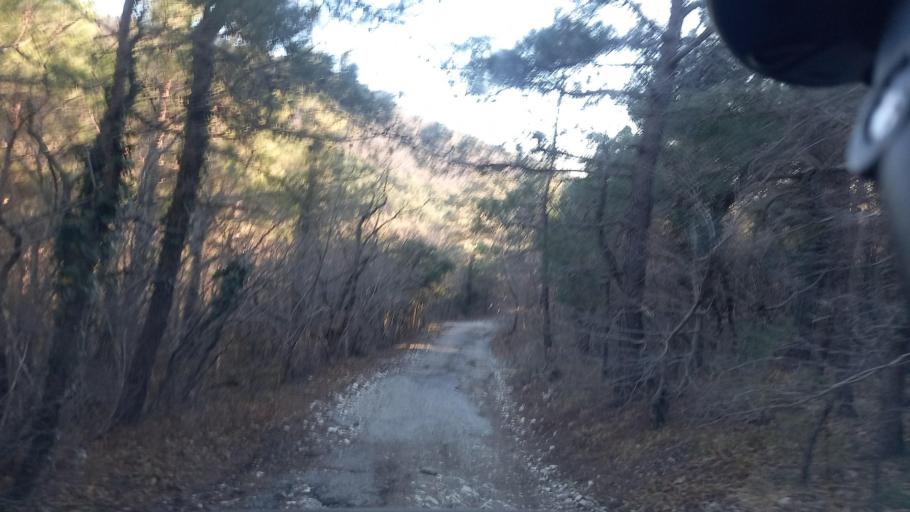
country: RU
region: Krasnodarskiy
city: Kabardinka
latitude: 44.6109
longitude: 37.9408
